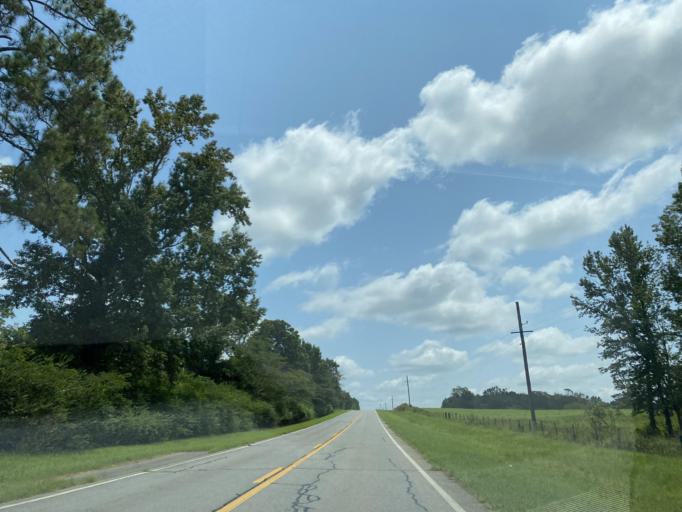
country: US
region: Georgia
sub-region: Telfair County
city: Helena
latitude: 32.0107
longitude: -83.1035
